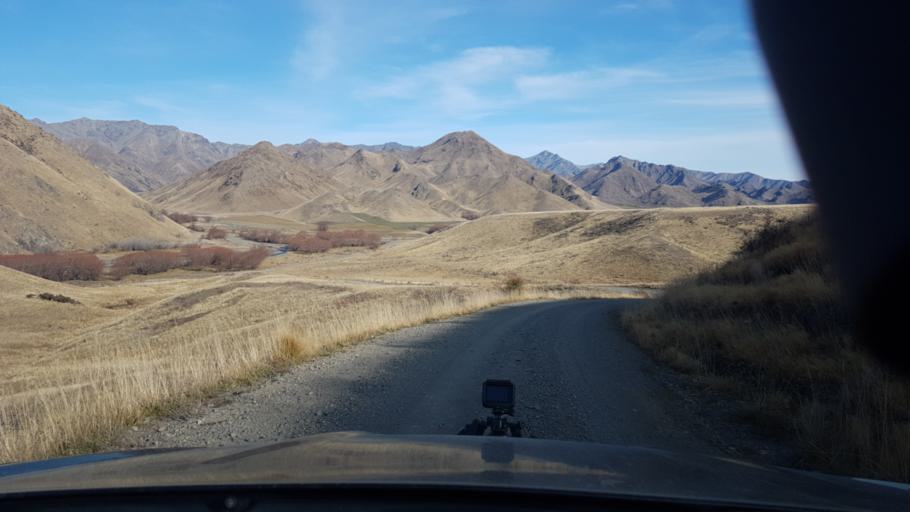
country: NZ
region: Canterbury
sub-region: Kaikoura District
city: Kaikoura
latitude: -42.0505
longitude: 173.3356
